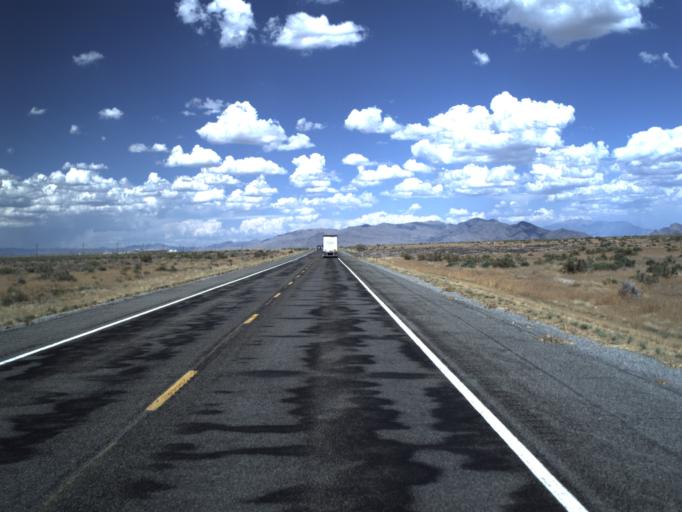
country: US
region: Utah
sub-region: Millard County
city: Delta
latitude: 39.4408
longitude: -112.4555
